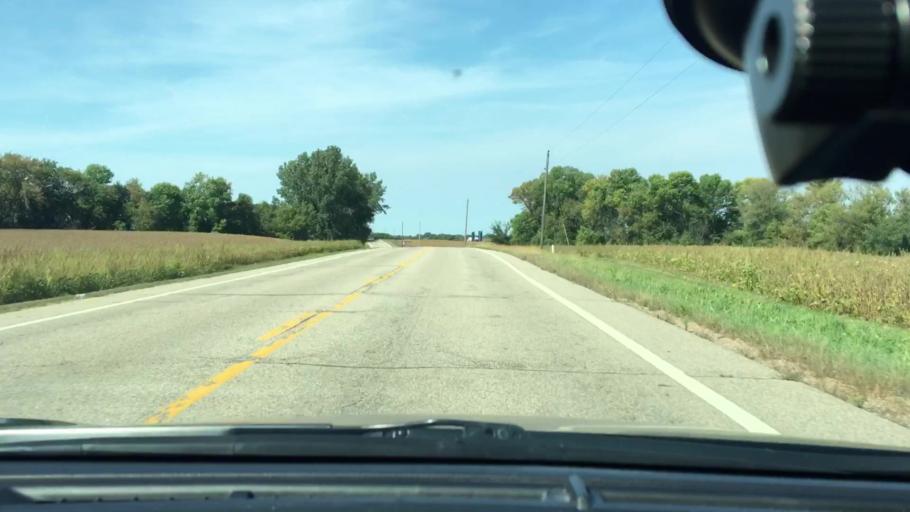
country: US
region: Minnesota
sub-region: Hennepin County
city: Corcoran
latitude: 45.1153
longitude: -93.5877
